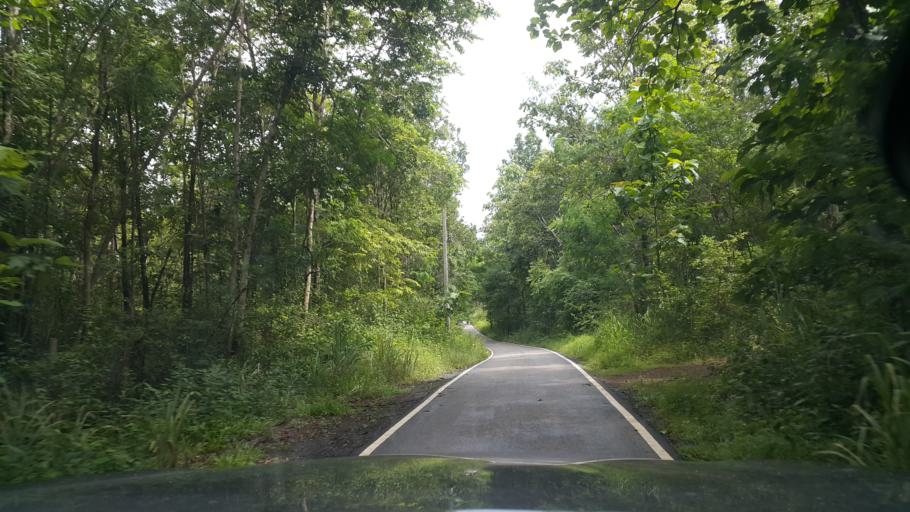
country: TH
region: Chiang Mai
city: Mae On
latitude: 18.8479
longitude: 99.2246
